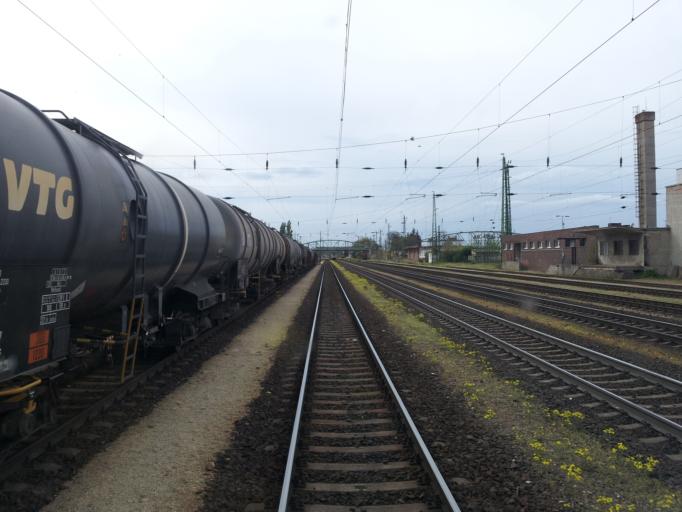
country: HU
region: Komarom-Esztergom
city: Komarom
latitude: 47.7482
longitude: 18.1257
